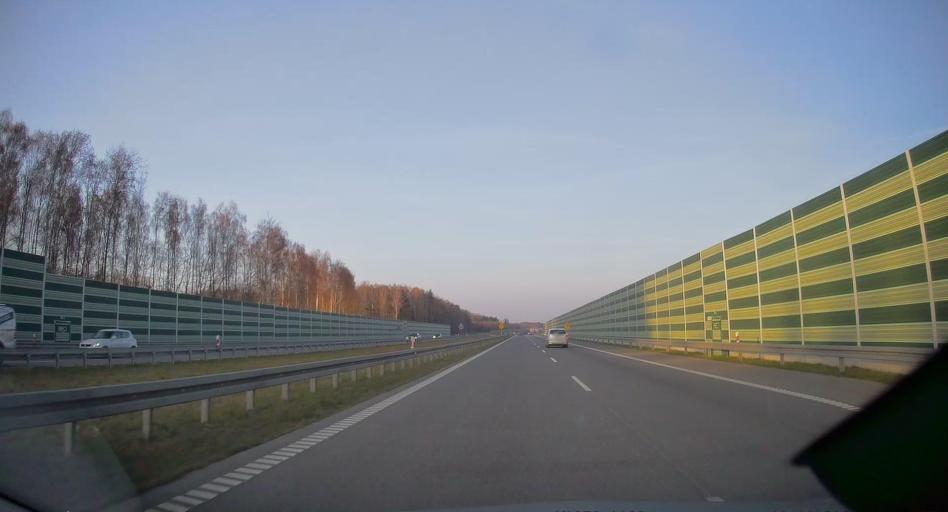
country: PL
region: Silesian Voivodeship
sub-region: Powiat czestochowski
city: Starcza
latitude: 50.6449
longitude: 19.0368
